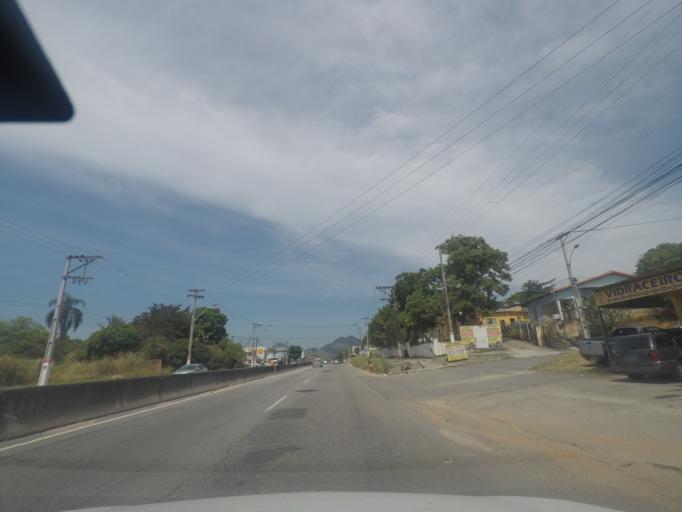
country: BR
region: Rio de Janeiro
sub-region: Marica
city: Marica
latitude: -22.9081
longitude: -42.8306
